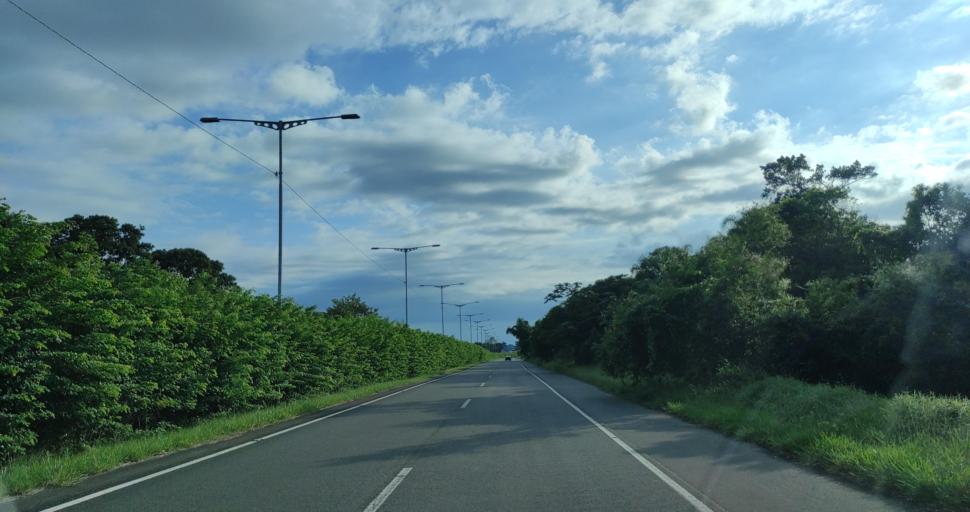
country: BR
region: Santa Catarina
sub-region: Penha
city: Penha
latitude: -26.8006
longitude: -48.6278
